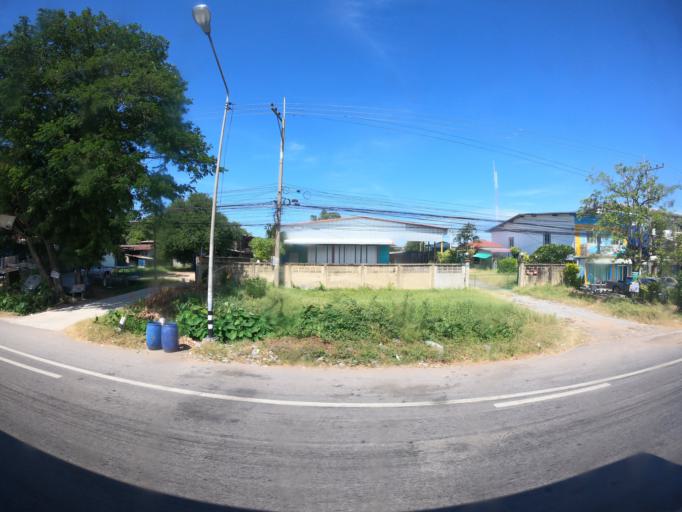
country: TH
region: Nakhon Ratchasima
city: Nakhon Ratchasima
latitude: 15.0329
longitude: 102.1423
